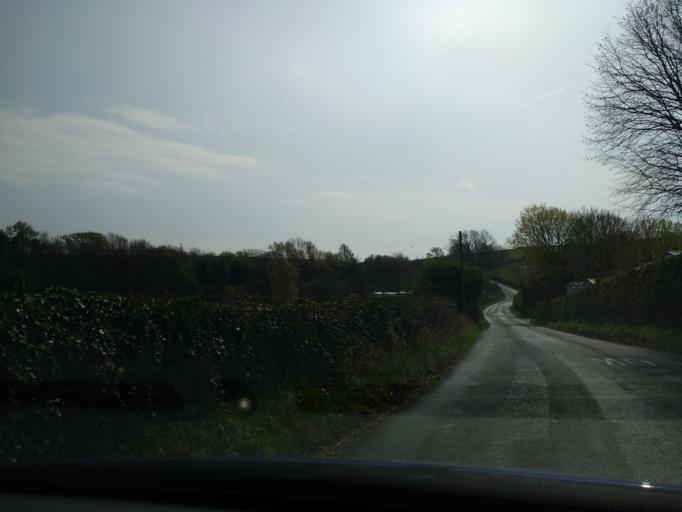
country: GB
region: England
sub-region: Lancashire
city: Bolton le Sands
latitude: 54.0862
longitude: -2.7966
